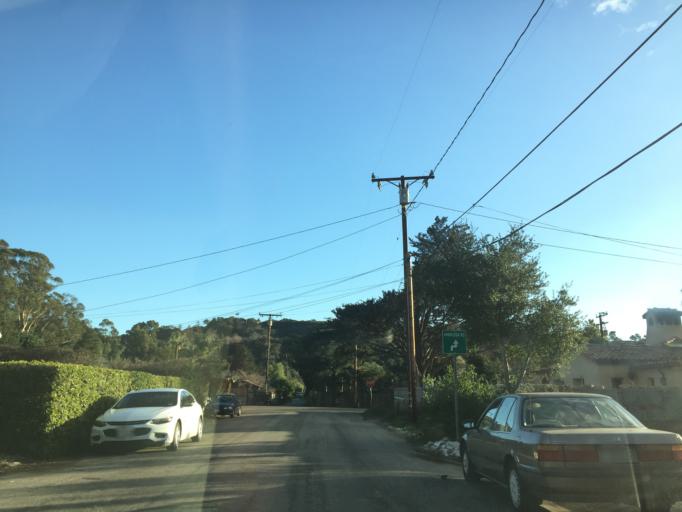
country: US
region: California
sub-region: Santa Barbara County
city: Goleta
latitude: 34.4370
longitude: -119.7731
